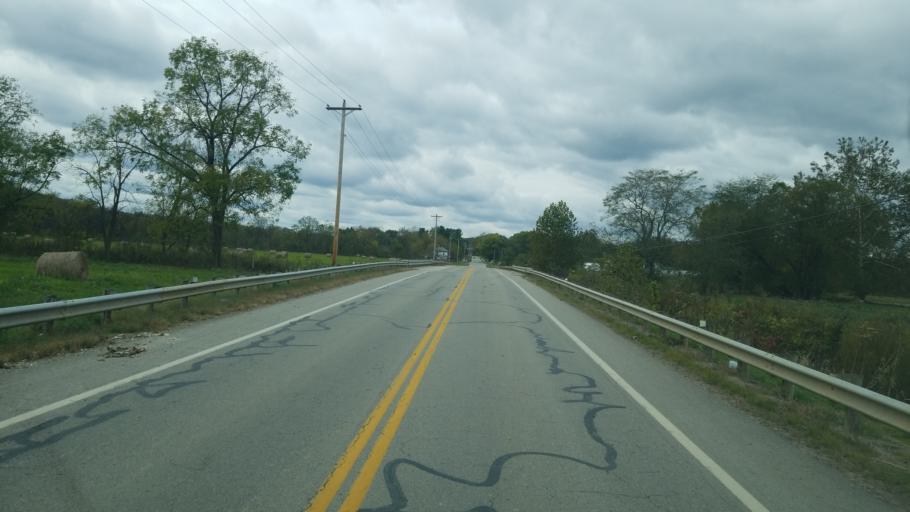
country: US
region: Ohio
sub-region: Jackson County
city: Wellston
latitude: 39.1598
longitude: -82.5110
